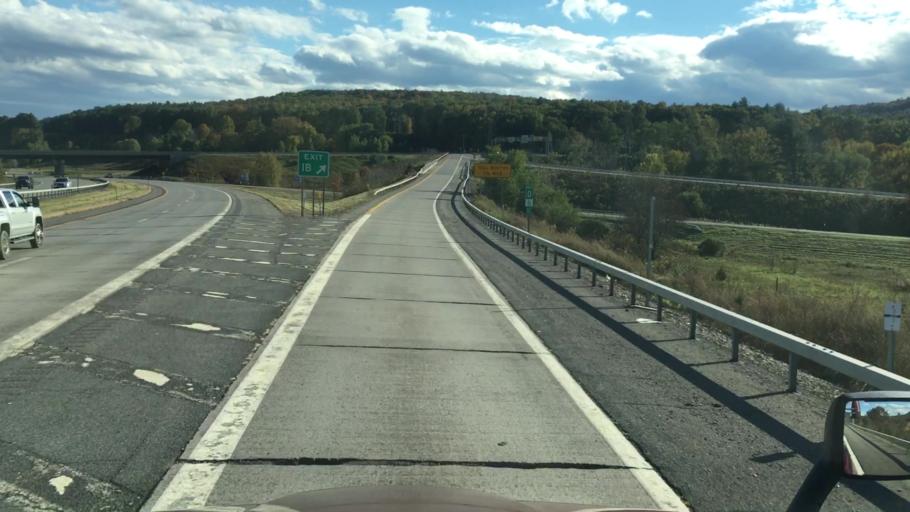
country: US
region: New York
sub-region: Schenectady County
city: Scotia
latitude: 42.8445
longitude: -74.0065
